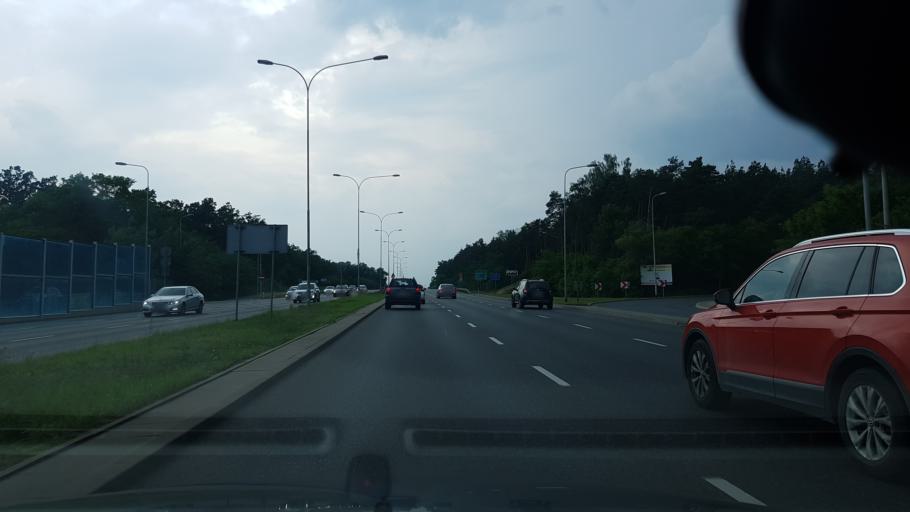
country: PL
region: Masovian Voivodeship
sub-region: Powiat legionowski
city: Jablonna
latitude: 52.3573
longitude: 20.9402
